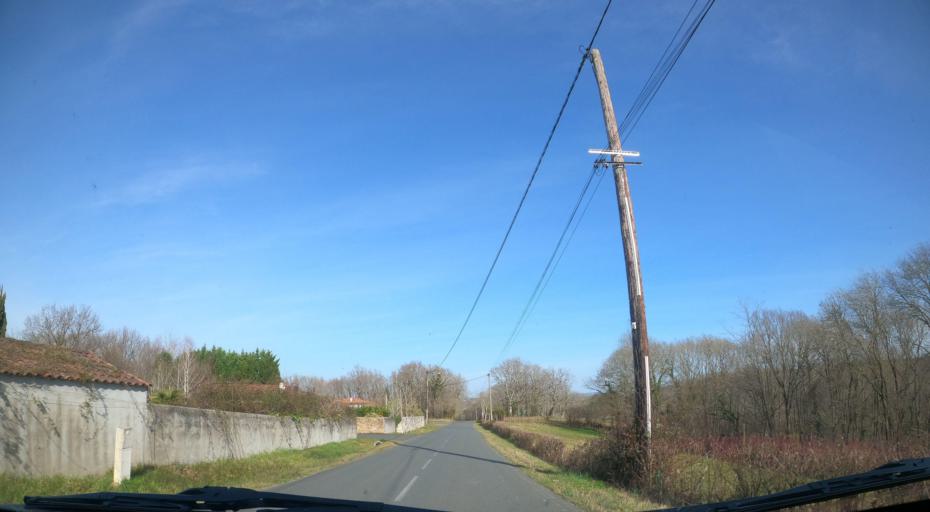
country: FR
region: Aquitaine
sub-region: Departement des Pyrenees-Atlantiques
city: Briscous
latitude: 43.4403
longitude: -1.3733
